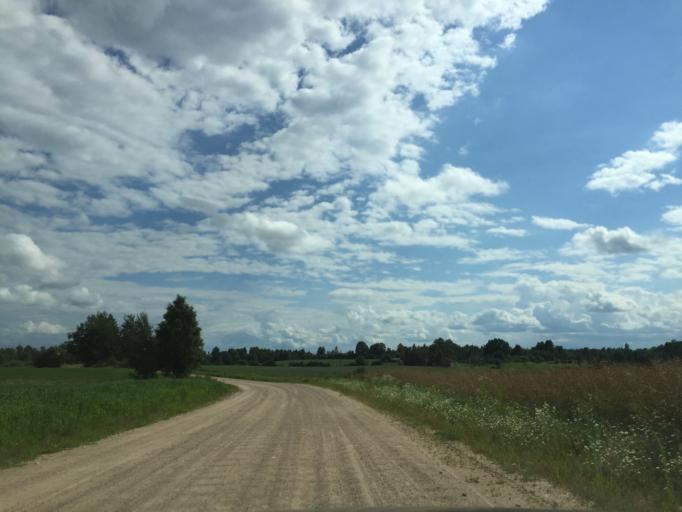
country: LV
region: Malpils
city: Malpils
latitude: 56.8513
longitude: 25.0489
